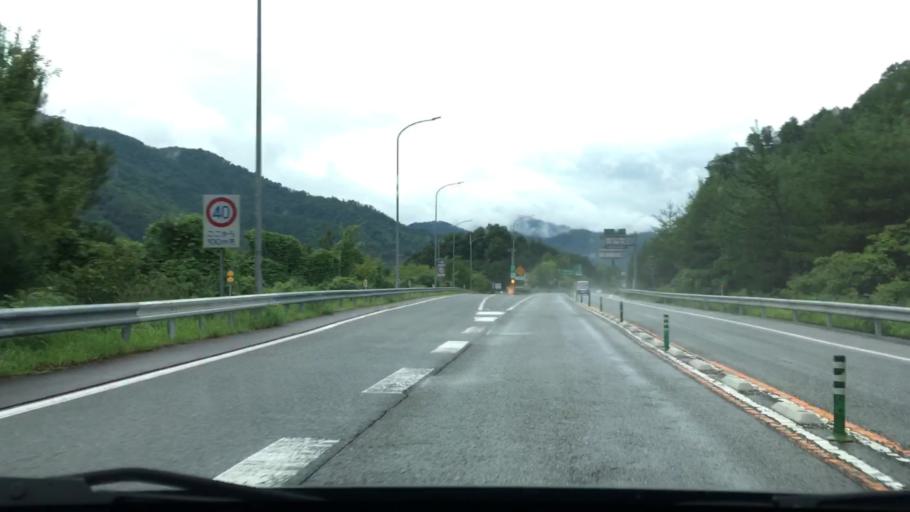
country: JP
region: Hyogo
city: Toyooka
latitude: 35.2971
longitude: 134.8254
